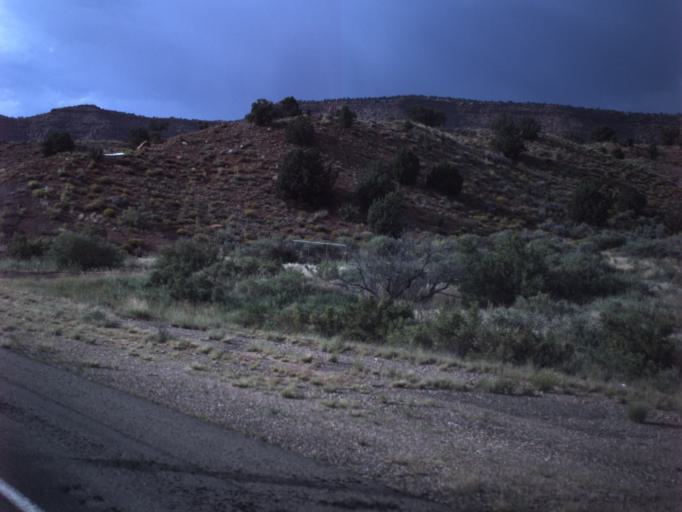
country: US
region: Utah
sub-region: Kane County
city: Kanab
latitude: 37.0349
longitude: -112.4994
